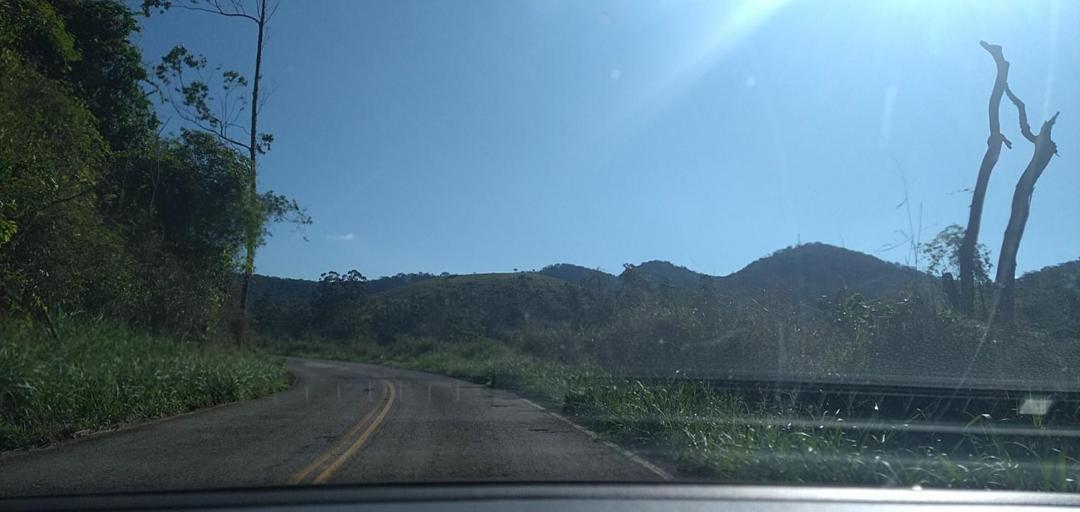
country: BR
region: Minas Gerais
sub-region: Alvinopolis
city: Alvinopolis
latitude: -20.1868
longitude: -42.9371
